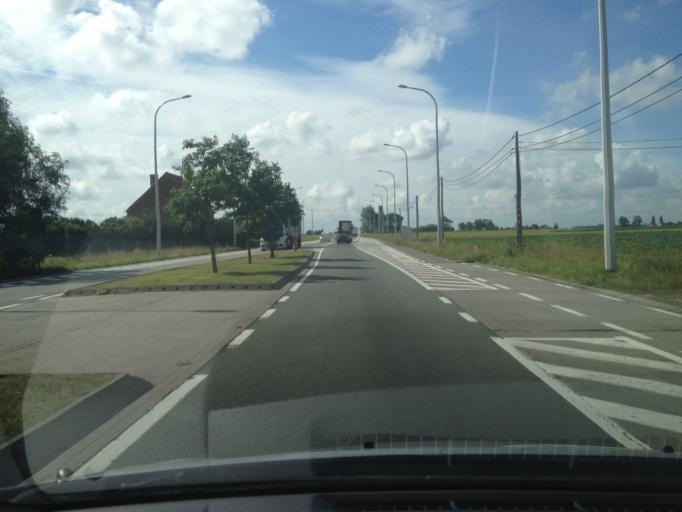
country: BE
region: Flanders
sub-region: Provincie West-Vlaanderen
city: Alveringem
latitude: 51.0048
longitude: 2.6843
